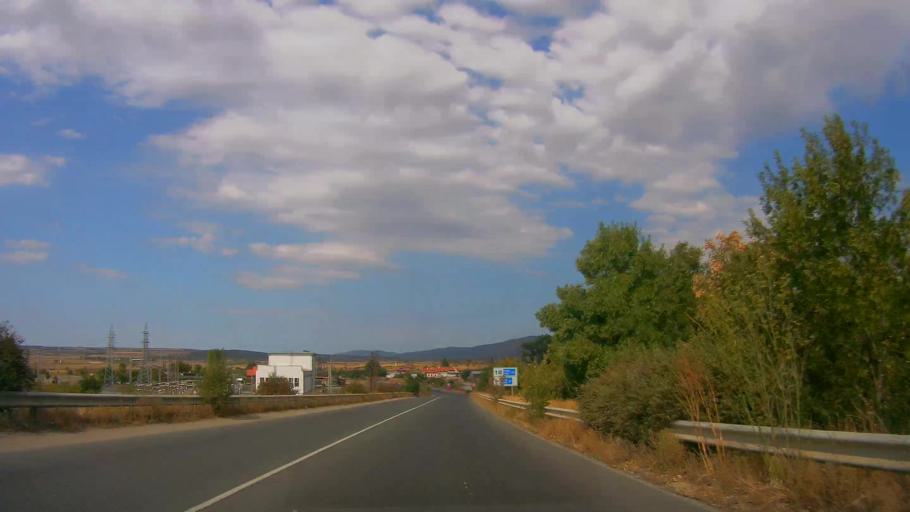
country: BG
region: Burgas
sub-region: Obshtina Aytos
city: Aytos
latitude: 42.7045
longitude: 27.2397
